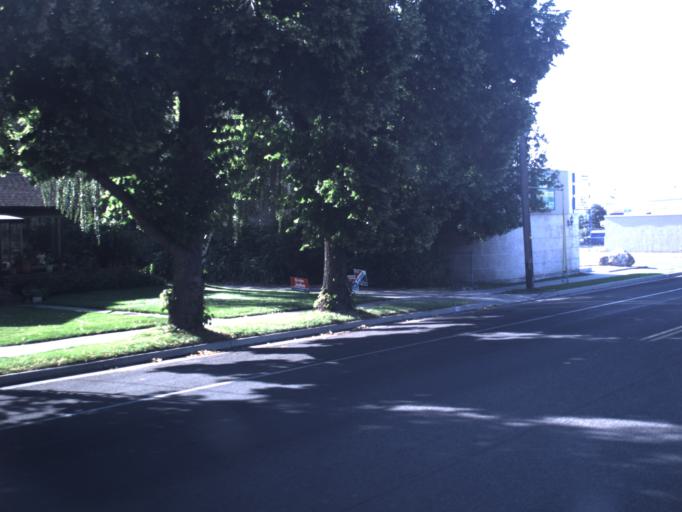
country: US
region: Utah
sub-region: Utah County
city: American Fork
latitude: 40.3802
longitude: -111.7959
